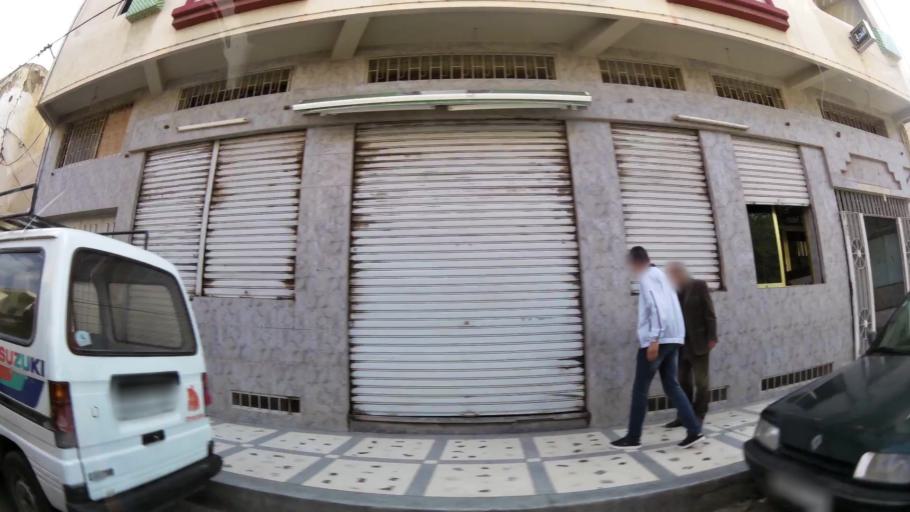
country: MA
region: Oriental
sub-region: Oujda-Angad
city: Oujda
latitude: 34.6822
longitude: -1.9111
